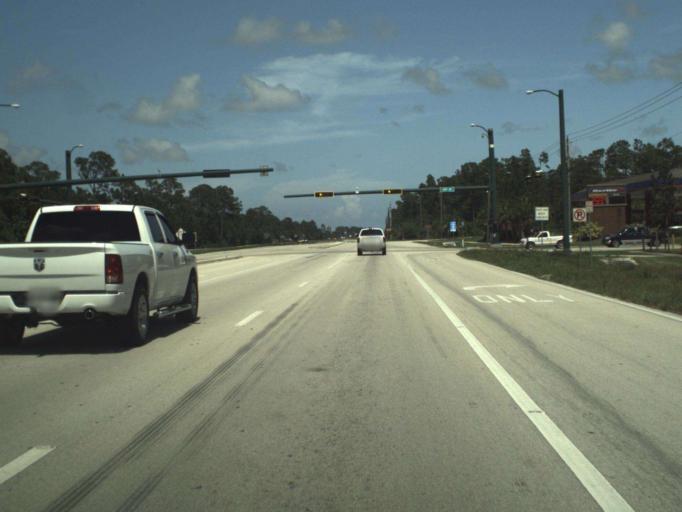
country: US
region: Florida
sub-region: Indian River County
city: Fellsmere
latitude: 27.7674
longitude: -80.5488
